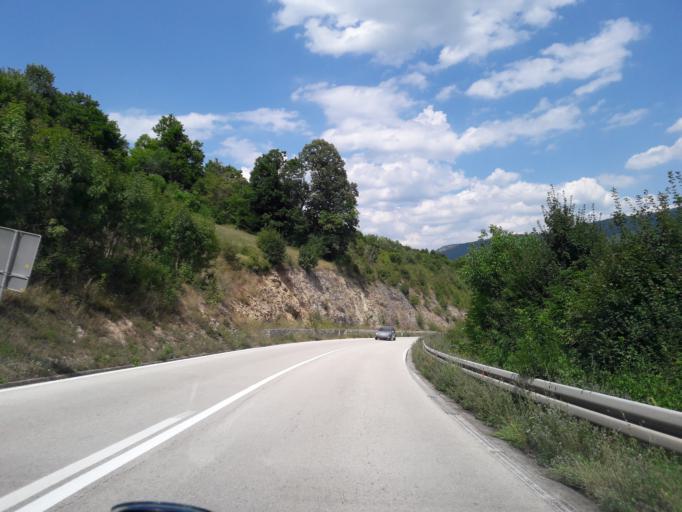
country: BA
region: Republika Srpska
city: Mrkonjic Grad
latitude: 44.5058
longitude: 17.1512
